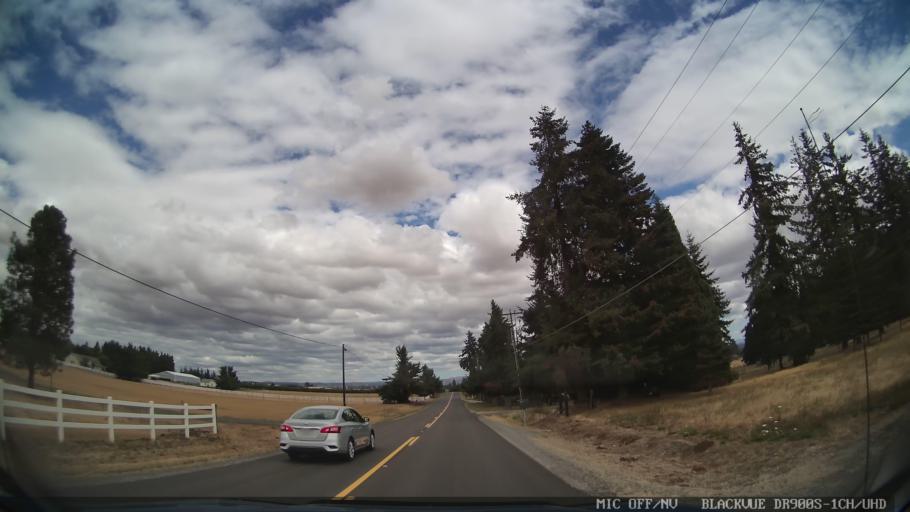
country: US
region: Oregon
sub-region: Marion County
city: Aumsville
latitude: 44.8604
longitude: -122.8577
